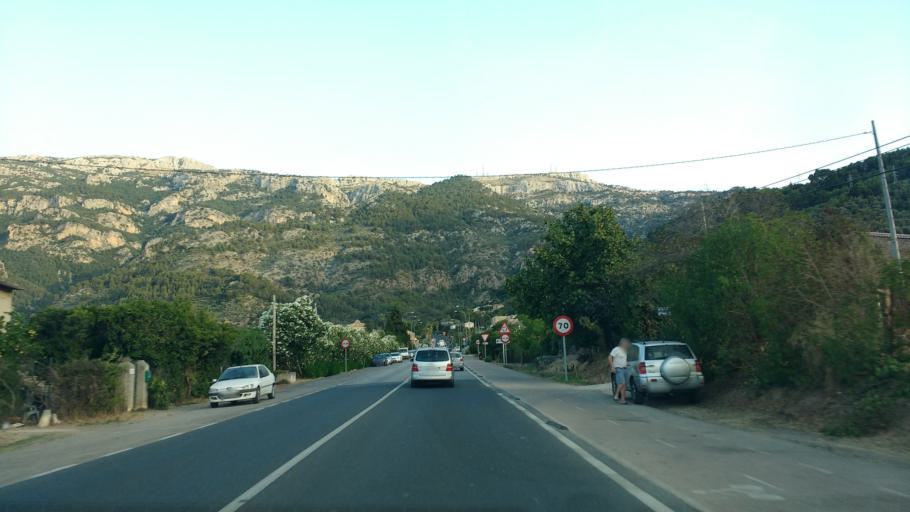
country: ES
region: Balearic Islands
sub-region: Illes Balears
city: Soller
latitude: 39.7689
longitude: 2.7071
